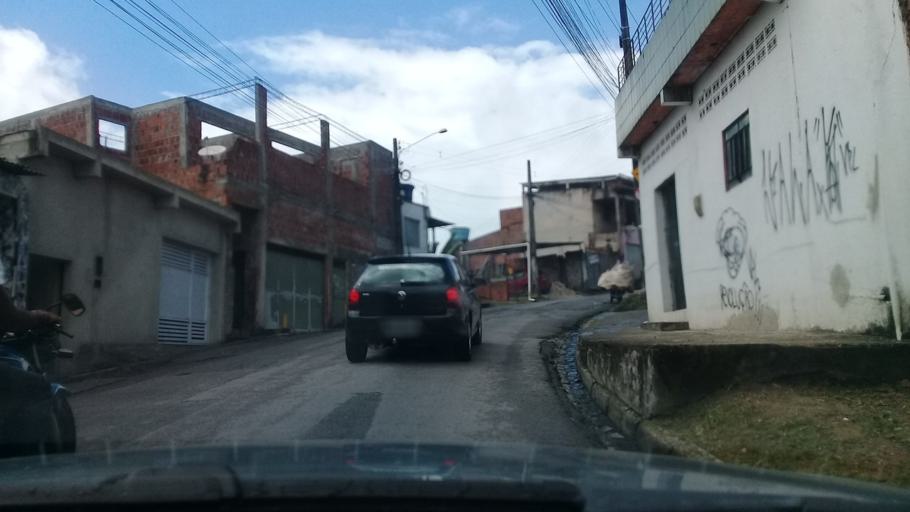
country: BR
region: Pernambuco
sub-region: Jaboatao Dos Guararapes
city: Jaboatao dos Guararapes
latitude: -8.1089
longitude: -34.9621
